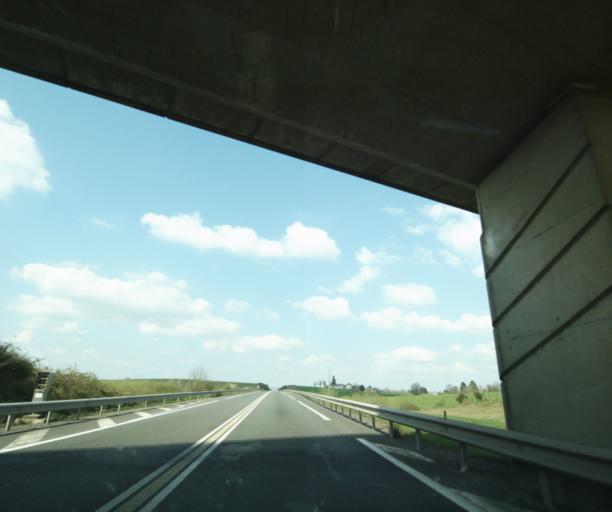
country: FR
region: Auvergne
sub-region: Departement de l'Allier
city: Montmarault
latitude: 46.3760
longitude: 3.0293
